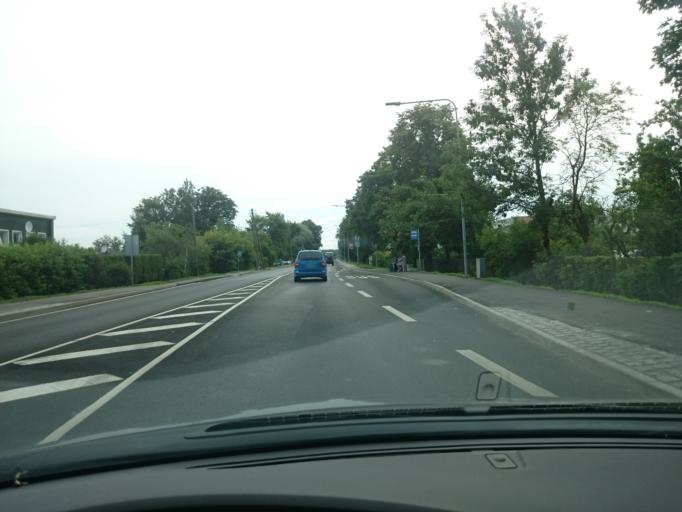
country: EE
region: Laeaene
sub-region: Haapsalu linn
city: Haapsalu
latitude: 58.9381
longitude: 23.5523
